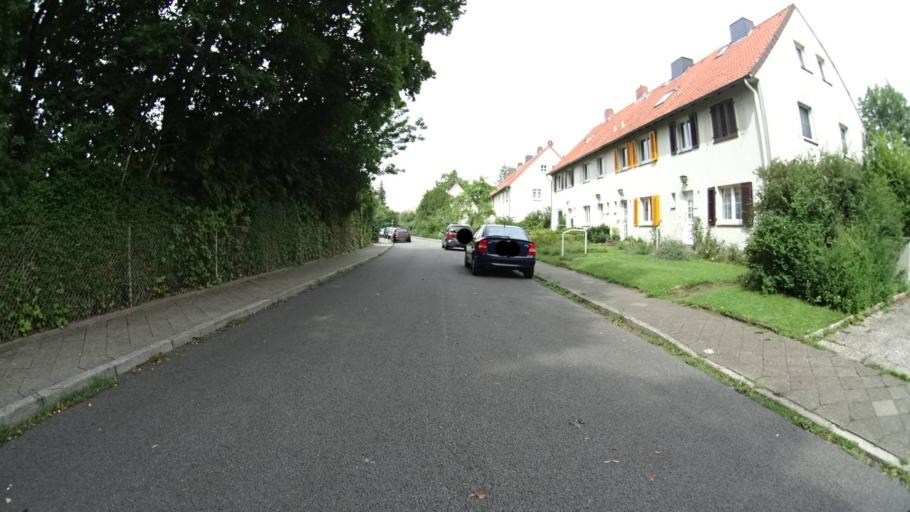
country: DE
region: Lower Saxony
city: Lueneburg
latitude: 53.2373
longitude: 10.4064
